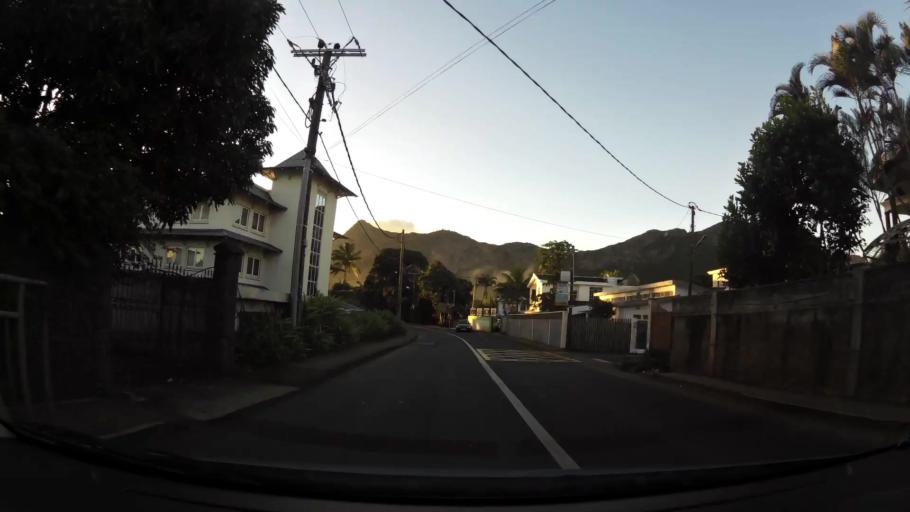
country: MU
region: Moka
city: Moka
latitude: -20.2253
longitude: 57.5067
